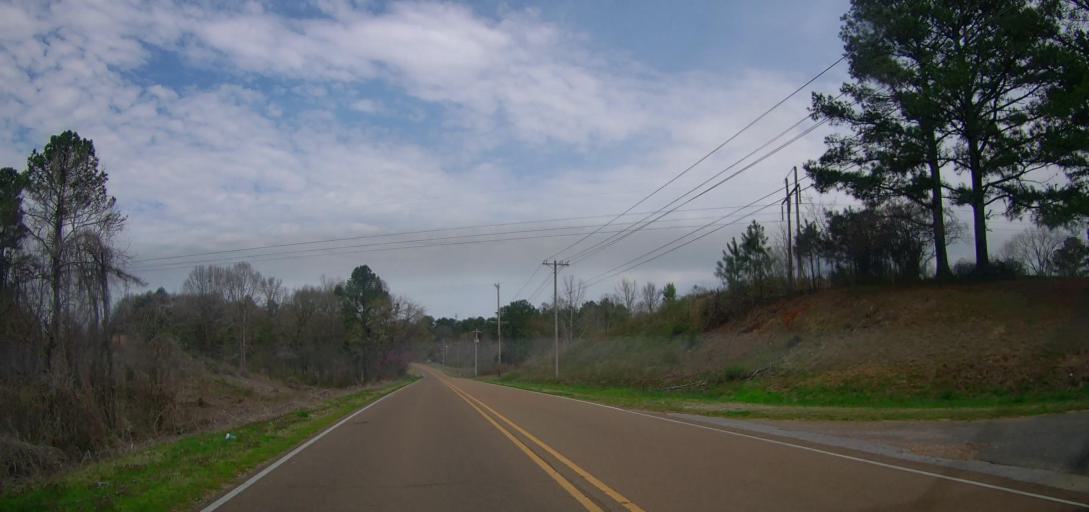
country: US
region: Mississippi
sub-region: Marshall County
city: Holly Springs
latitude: 34.7548
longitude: -89.4297
